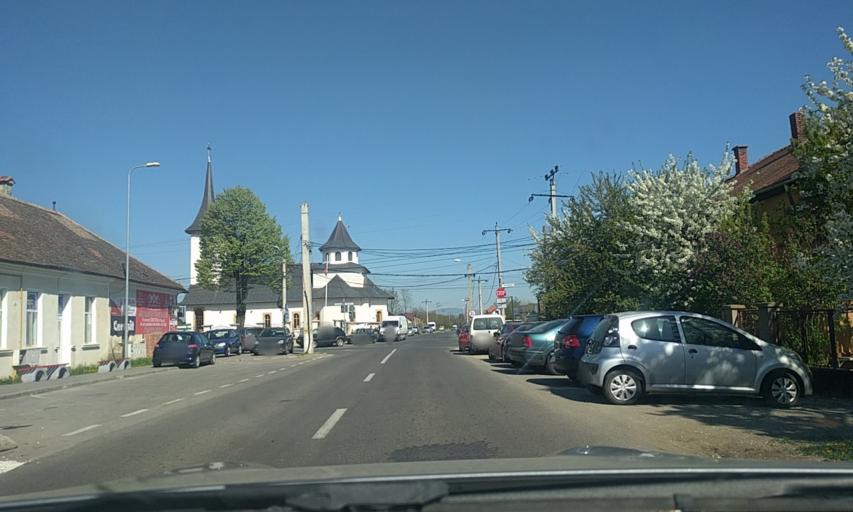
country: RO
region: Brasov
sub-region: Comuna Ghimbav
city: Ghimbav
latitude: 45.6978
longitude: 25.5586
